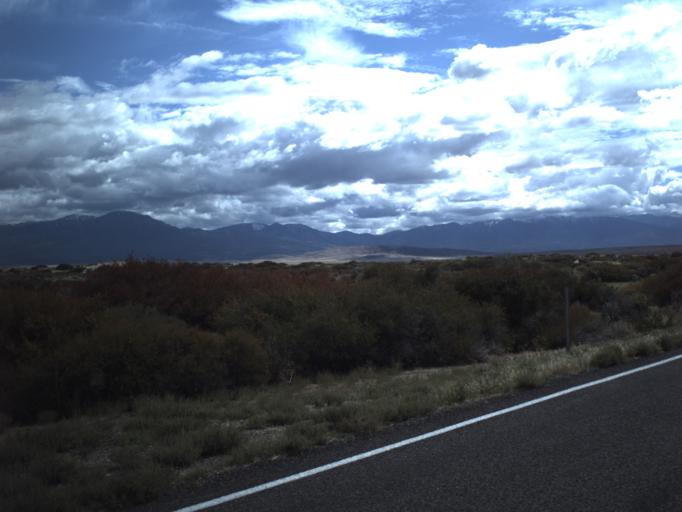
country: US
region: Utah
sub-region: Millard County
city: Fillmore
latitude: 39.1241
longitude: -112.4096
